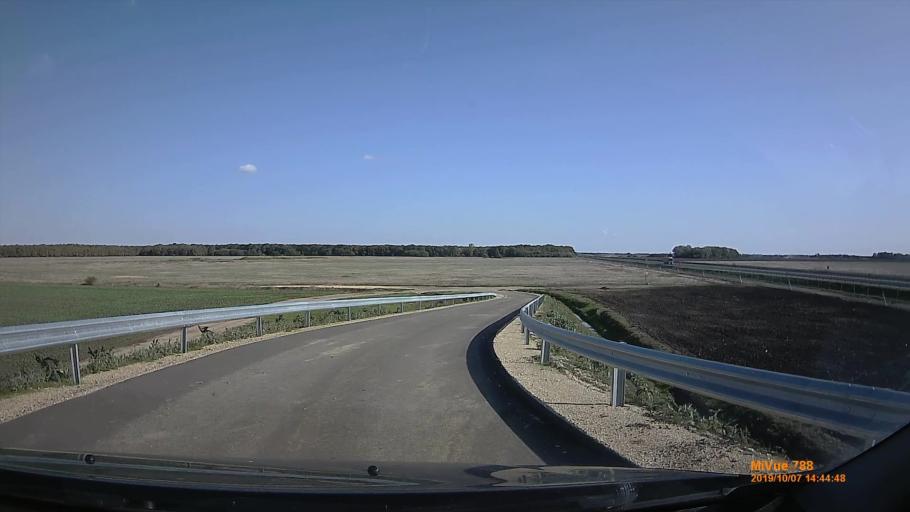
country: HU
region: Jasz-Nagykun-Szolnok
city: Kunszentmarton
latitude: 46.8537
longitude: 20.3176
